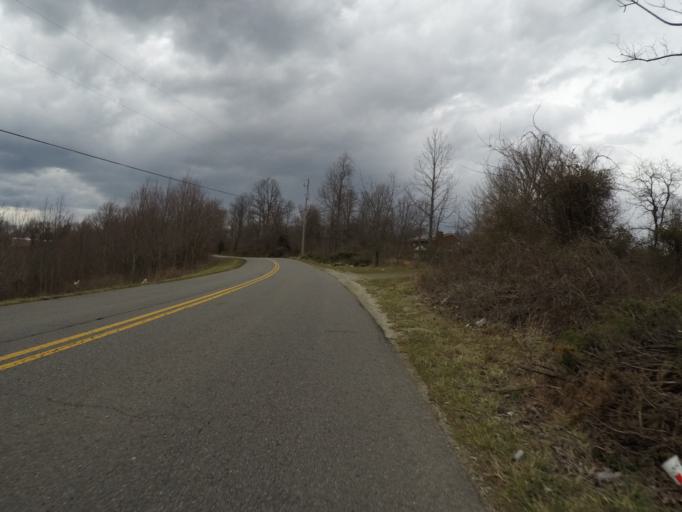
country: US
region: Ohio
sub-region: Lawrence County
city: Burlington
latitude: 38.4375
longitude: -82.5288
